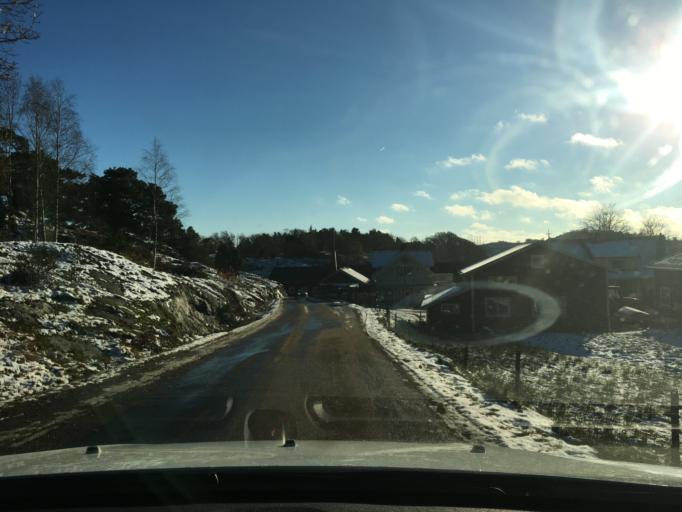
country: SE
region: Vaestra Goetaland
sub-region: Tjorns Kommun
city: Myggenas
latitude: 58.0899
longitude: 11.7501
